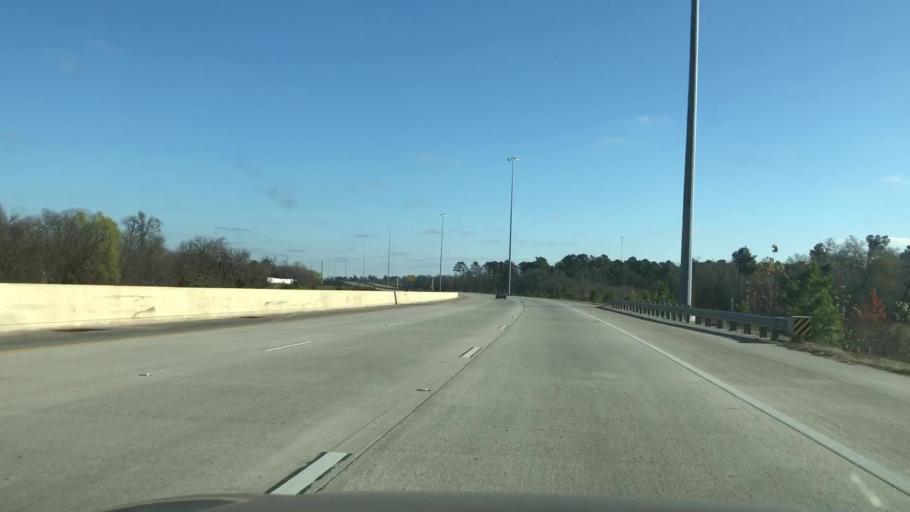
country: US
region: Texas
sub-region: Harris County
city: Jacinto City
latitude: 29.7946
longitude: -95.2293
